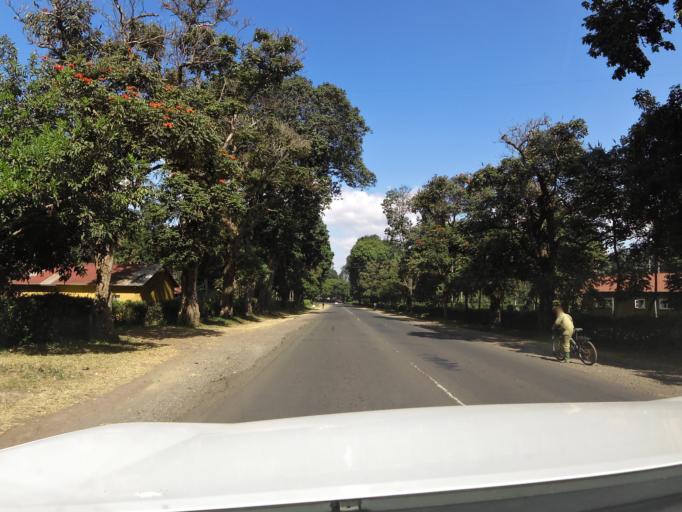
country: TZ
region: Arusha
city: Arusha
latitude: -3.3712
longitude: 36.6418
